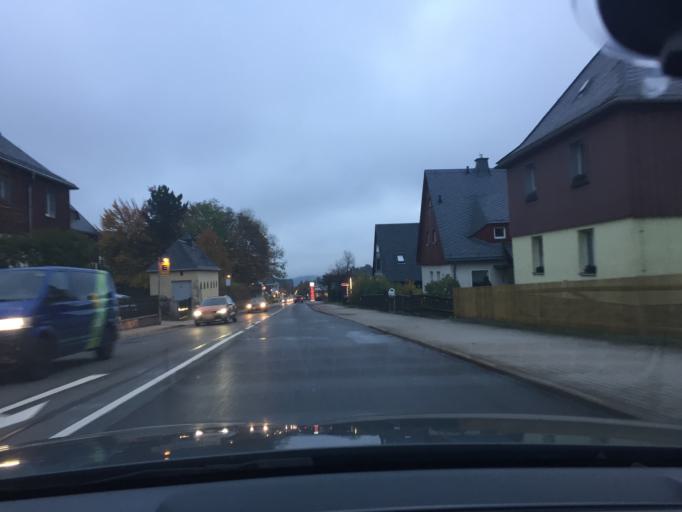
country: DE
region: Saxony
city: Altenberg
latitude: 50.7653
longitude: 13.7542
